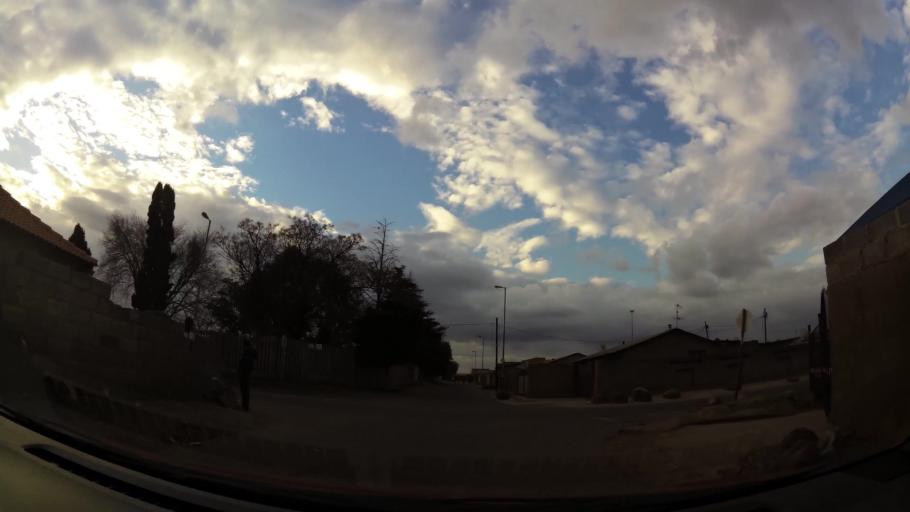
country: ZA
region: Gauteng
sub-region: City of Johannesburg Metropolitan Municipality
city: Soweto
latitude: -26.2469
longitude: 27.8279
